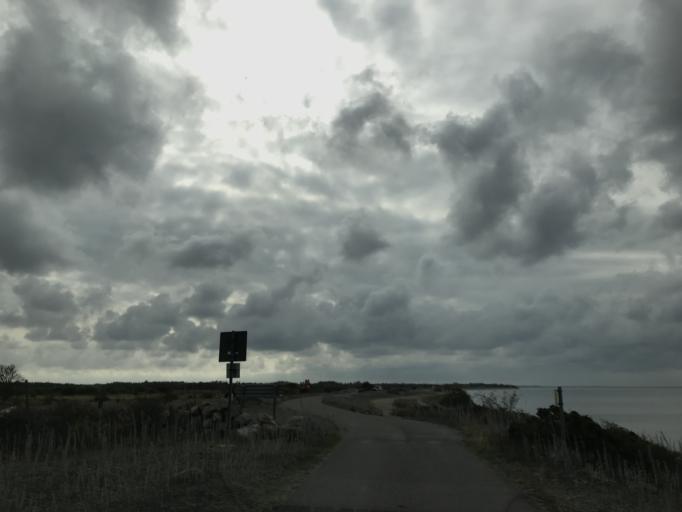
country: SE
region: Kalmar
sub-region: Borgholms Kommun
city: Borgholm
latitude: 57.0564
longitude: 16.8371
